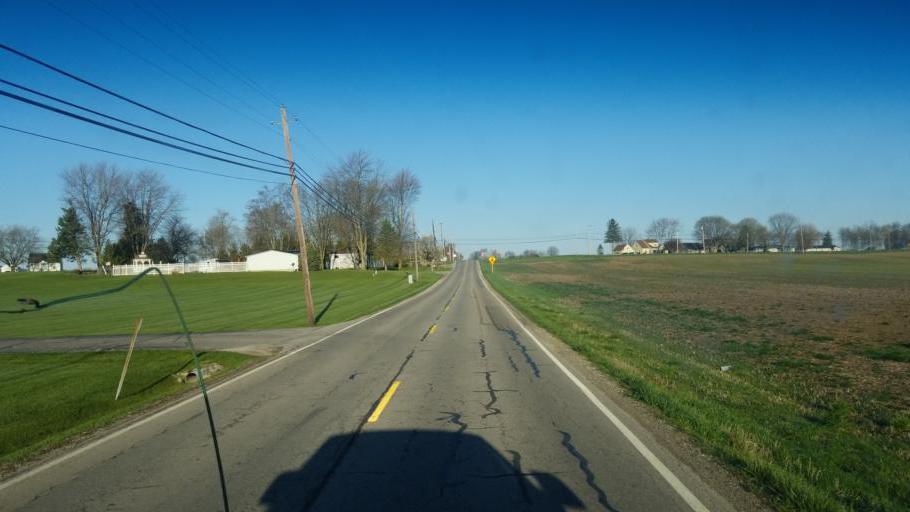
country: US
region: Ohio
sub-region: Marion County
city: Marion
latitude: 40.5349
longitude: -83.1039
